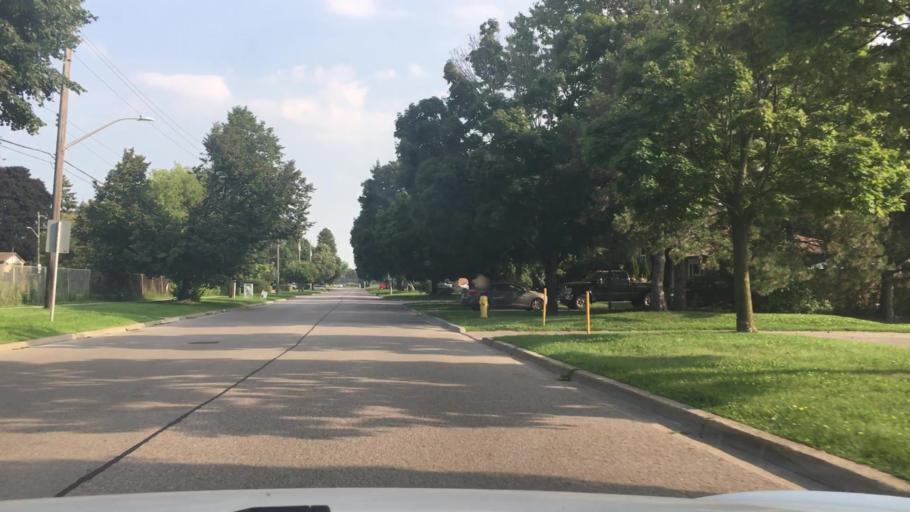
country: CA
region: Ontario
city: Ajax
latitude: 43.8720
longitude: -78.9496
